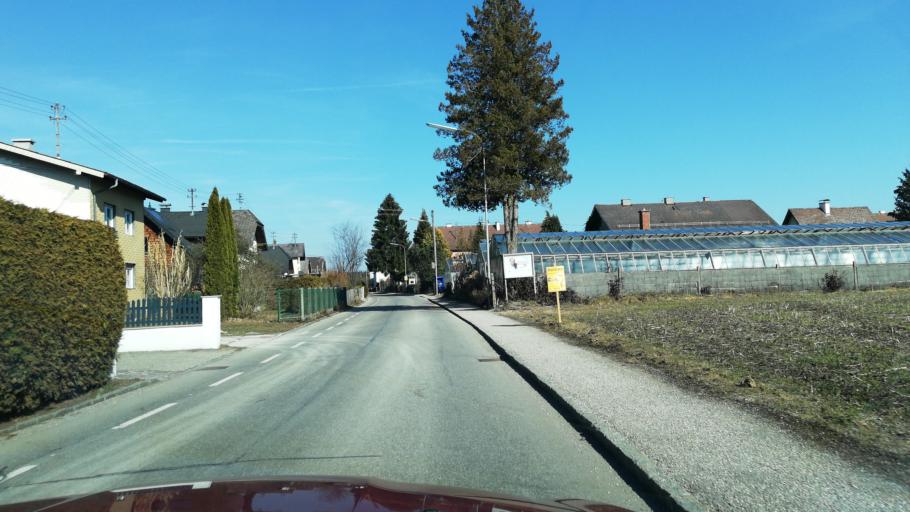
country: AT
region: Upper Austria
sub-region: Politischer Bezirk Vocklabruck
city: Redlham
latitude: 48.0159
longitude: 13.7315
